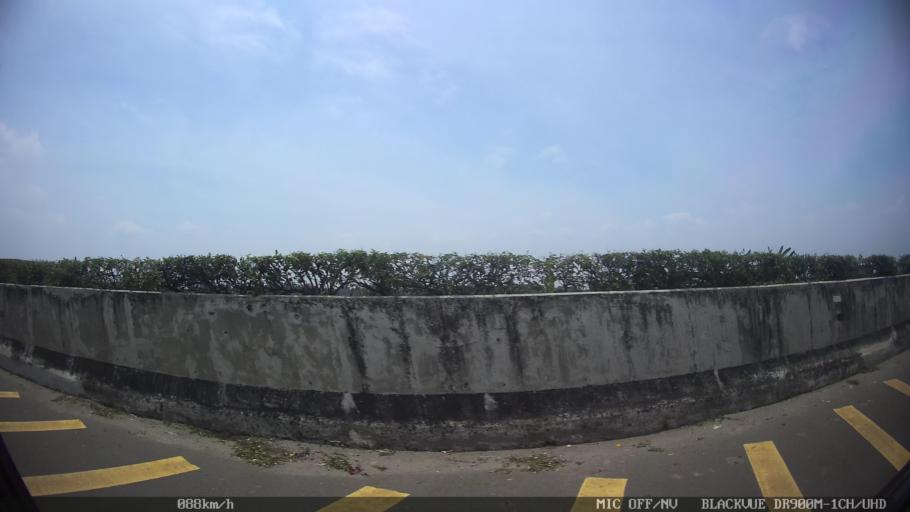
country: ID
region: West Java
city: Kresek
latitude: -6.1771
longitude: 106.3718
